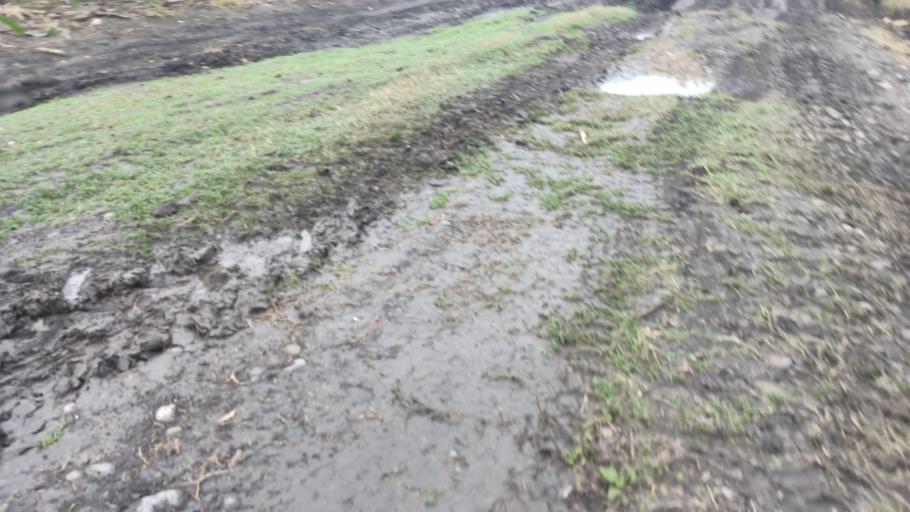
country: MX
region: Puebla
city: Espinal
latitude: 20.3065
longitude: -97.4130
